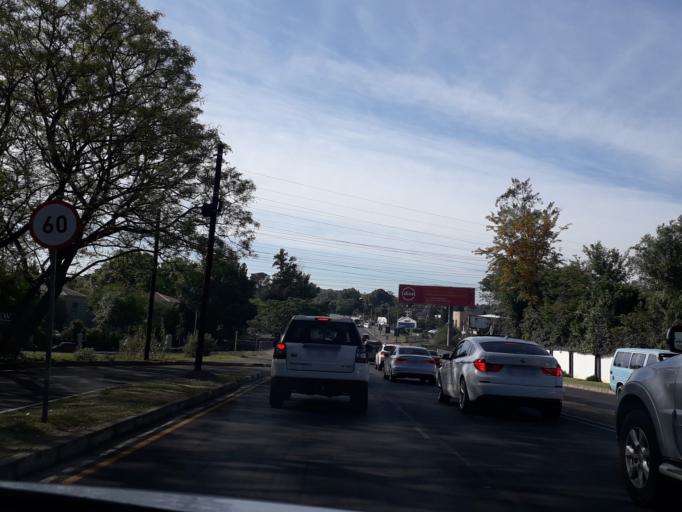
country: ZA
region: Gauteng
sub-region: City of Johannesburg Metropolitan Municipality
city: Johannesburg
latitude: -26.1117
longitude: 28.0192
